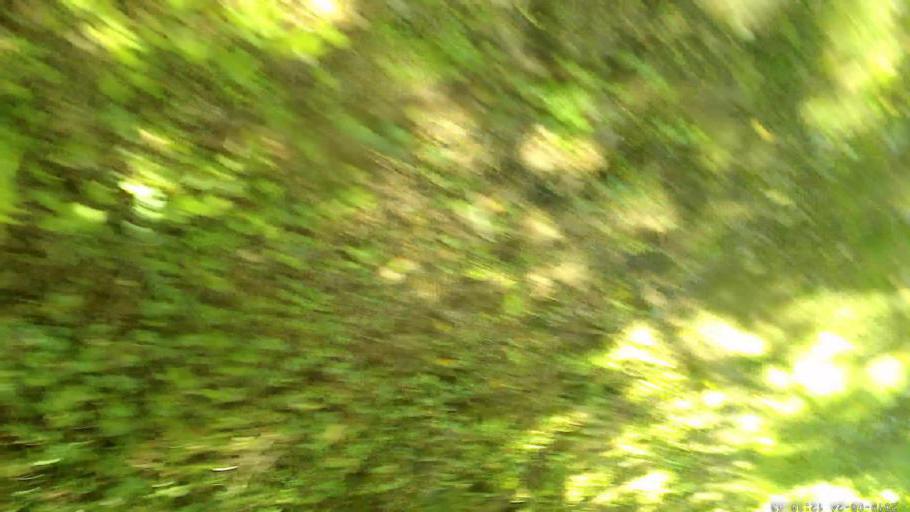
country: JP
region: Nagano
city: Komoro
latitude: 36.2660
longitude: 138.3678
